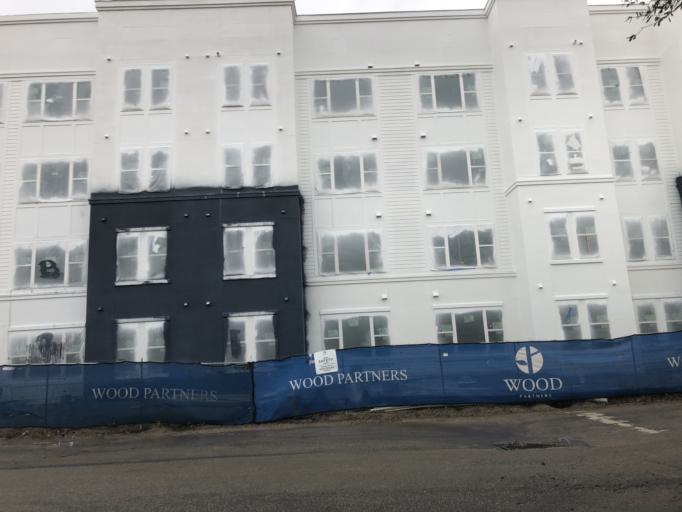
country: US
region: Florida
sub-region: Orange County
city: Doctor Phillips
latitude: 28.4532
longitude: -81.4785
